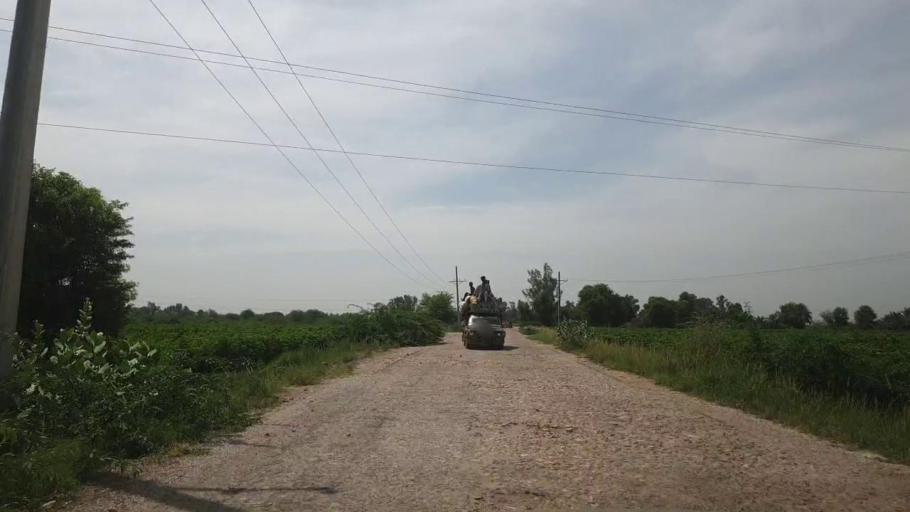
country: PK
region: Sindh
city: Kot Diji
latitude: 27.1283
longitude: 68.9981
